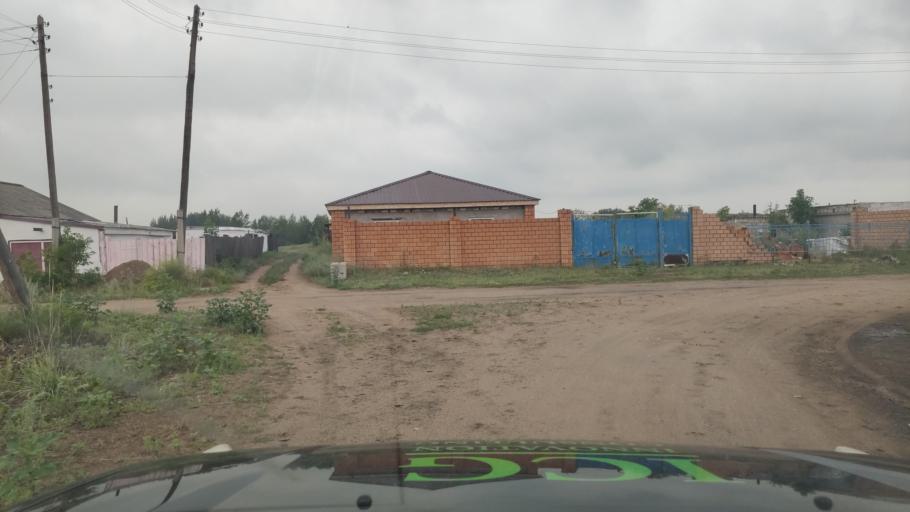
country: KZ
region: Pavlodar
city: Pavlodar
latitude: 52.1055
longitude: 77.0937
